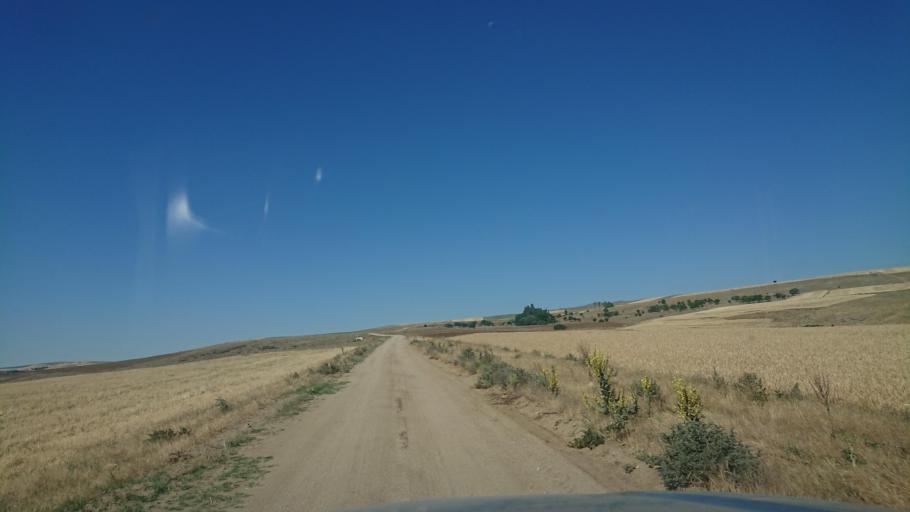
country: TR
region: Aksaray
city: Sariyahsi
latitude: 38.9368
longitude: 33.8660
